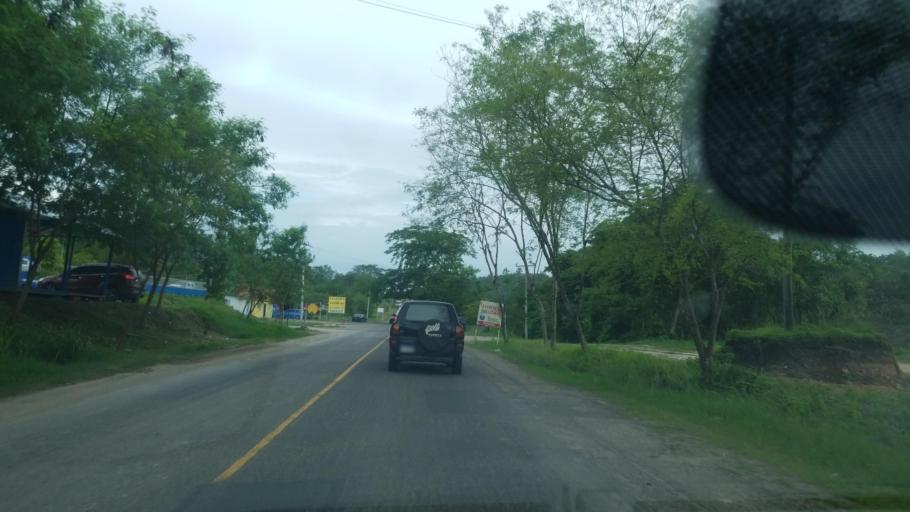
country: HN
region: Santa Barbara
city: Santa Barbara
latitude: 14.9069
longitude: -88.2530
